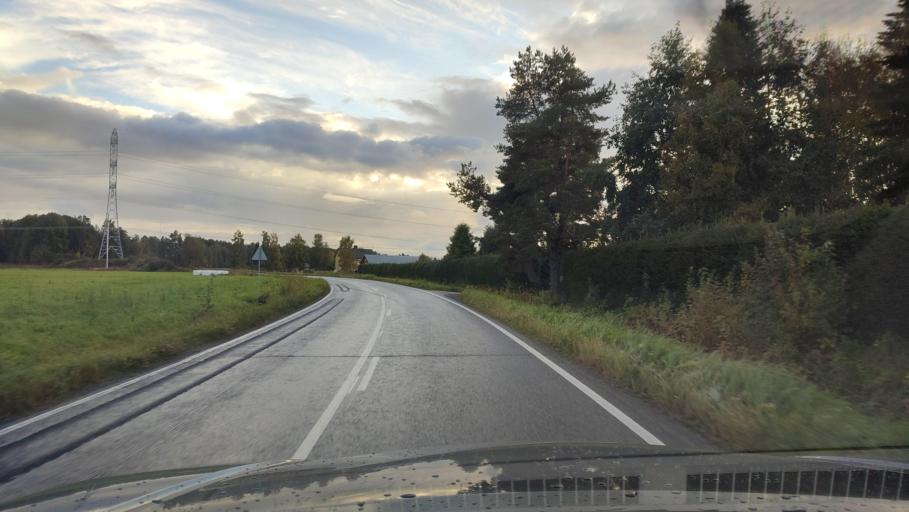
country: FI
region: Ostrobothnia
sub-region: Sydosterbotten
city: Kristinestad
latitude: 62.2888
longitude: 21.4246
